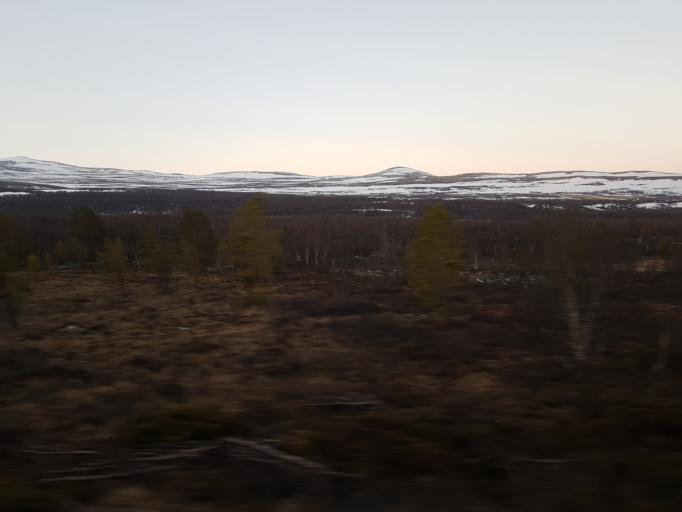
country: NO
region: Oppland
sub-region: Dovre
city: Dombas
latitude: 62.1025
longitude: 9.2192
